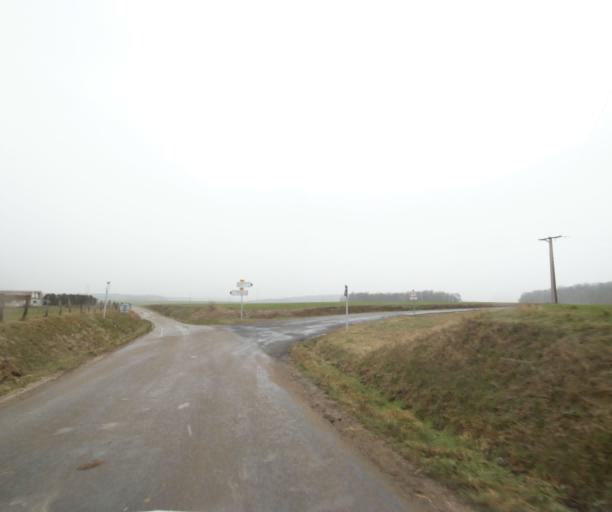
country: FR
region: Champagne-Ardenne
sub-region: Departement de la Haute-Marne
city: Bienville
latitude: 48.5281
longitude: 5.0446
